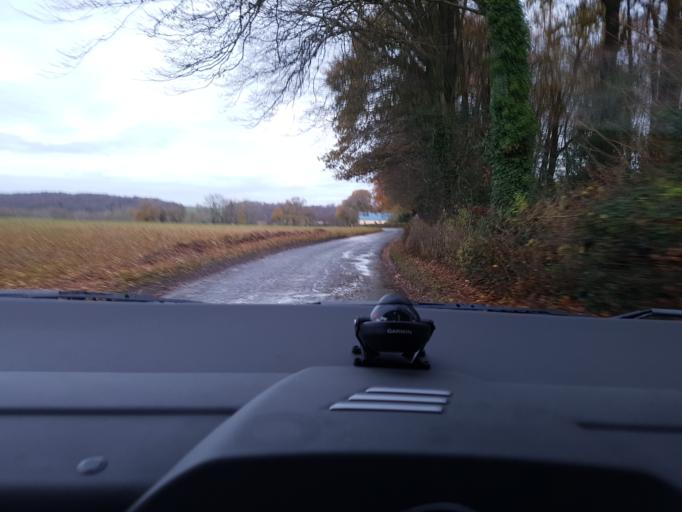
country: FR
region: Picardie
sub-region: Departement de l'Oise
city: Songeons
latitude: 49.5979
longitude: 1.8866
